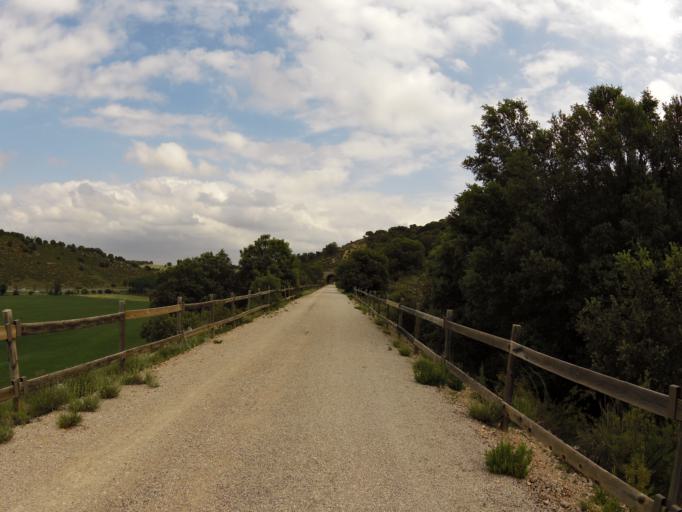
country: ES
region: Castille-La Mancha
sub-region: Provincia de Albacete
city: Robledo
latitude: 38.7767
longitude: -2.3905
